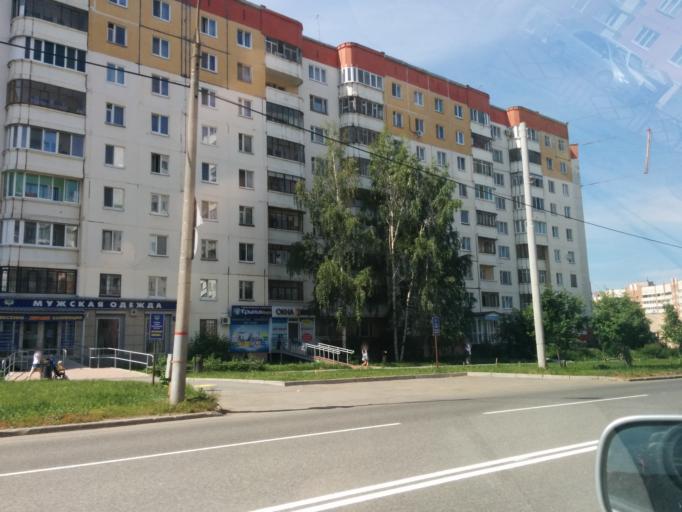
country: RU
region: Perm
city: Perm
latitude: 58.0040
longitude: 56.3056
